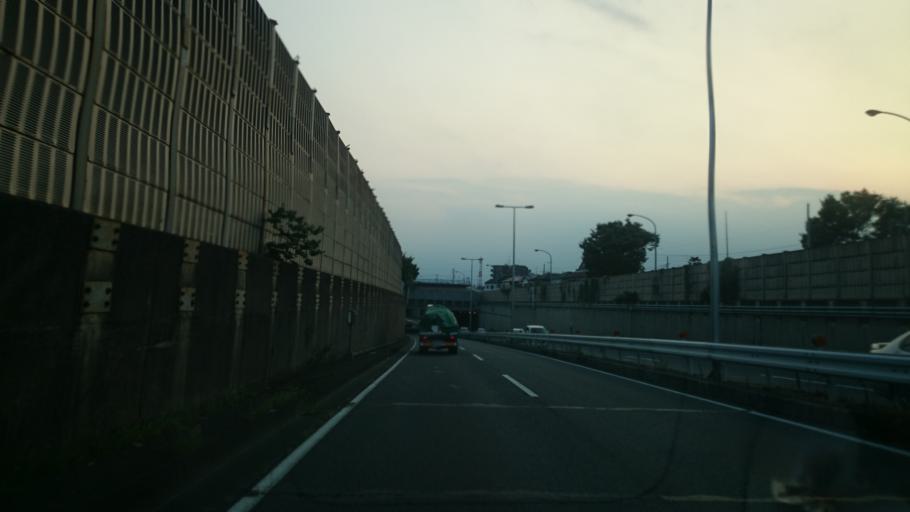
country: JP
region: Saitama
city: Ageoshimo
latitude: 35.9627
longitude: 139.6324
